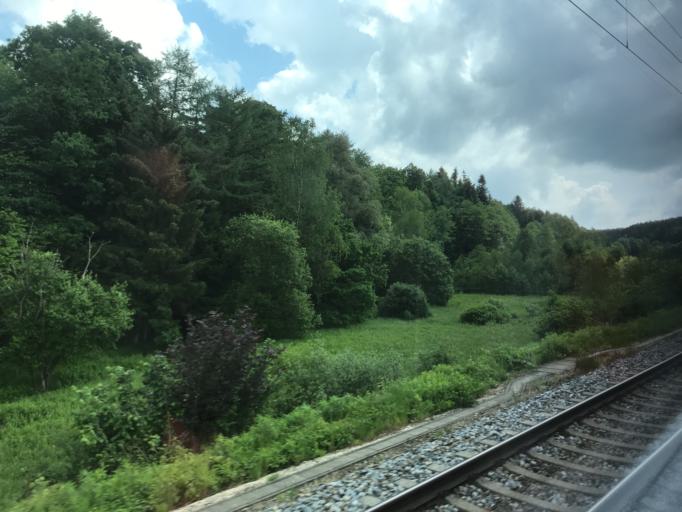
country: DE
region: Bavaria
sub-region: Swabia
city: Rosshaupten
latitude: 48.3884
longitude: 10.4963
